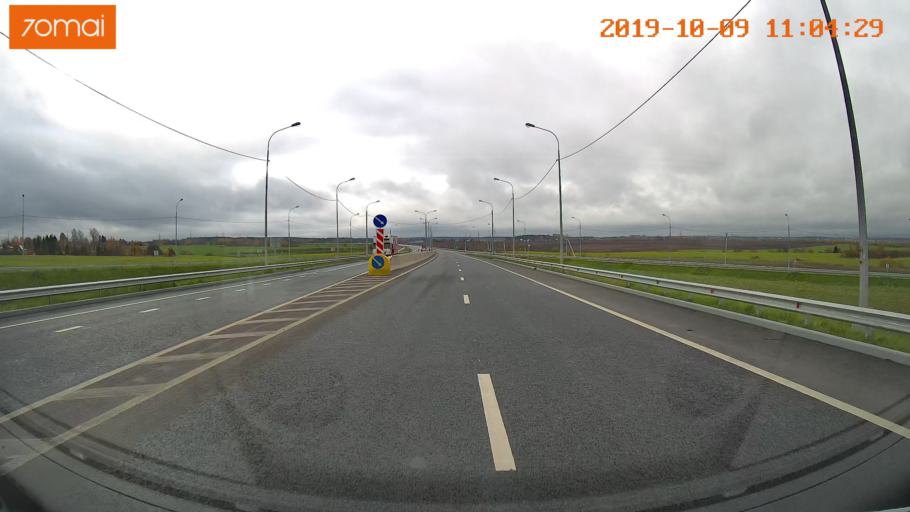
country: RU
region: Vologda
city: Vologda
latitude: 59.2117
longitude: 39.7670
